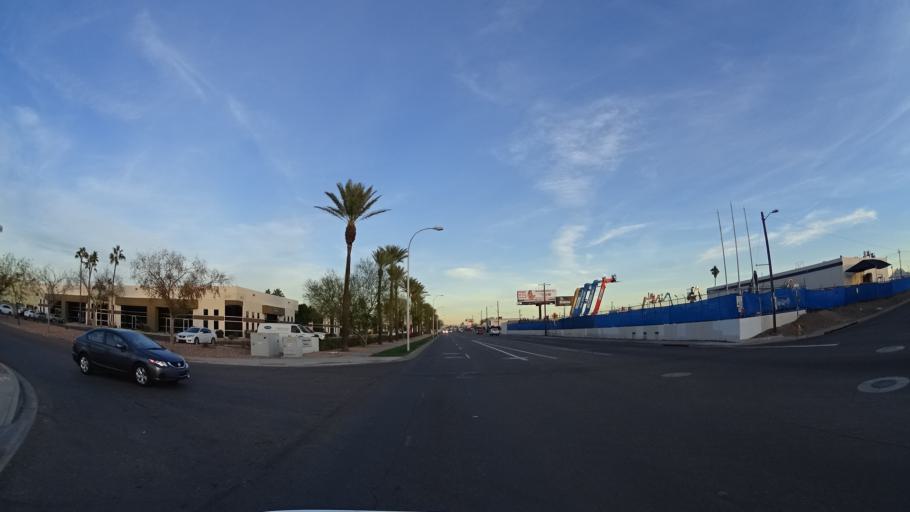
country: US
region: Arizona
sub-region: Maricopa County
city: Tempe Junction
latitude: 33.4221
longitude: -111.9999
